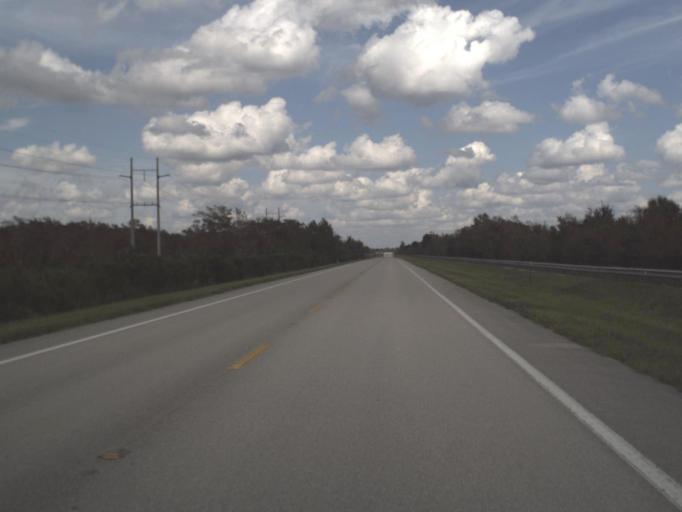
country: US
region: Florida
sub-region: Collier County
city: Lely Resort
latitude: 25.9700
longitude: -81.3522
